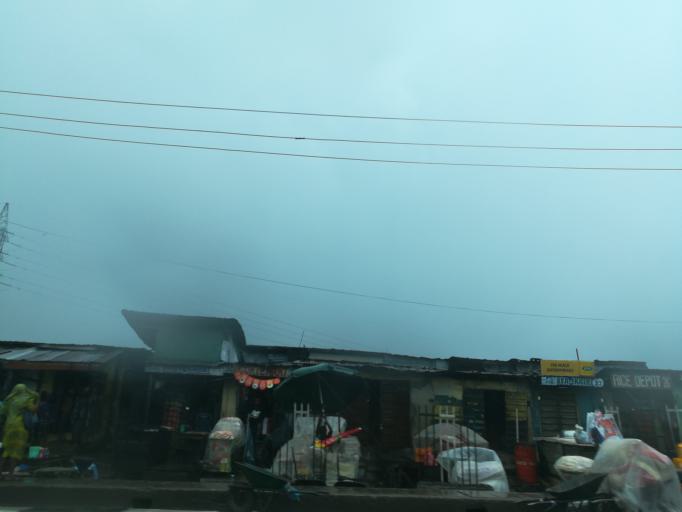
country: NG
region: Lagos
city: Ojota
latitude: 6.6079
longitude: 3.3967
